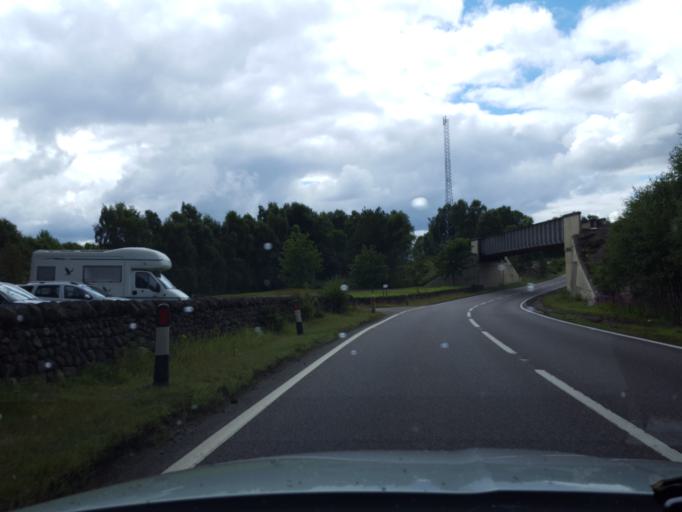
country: GB
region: Scotland
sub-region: Highland
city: Aviemore
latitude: 57.2351
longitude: -3.8069
